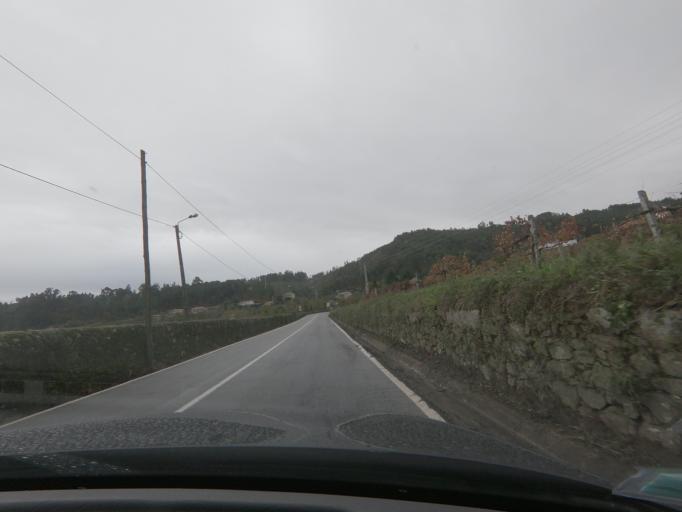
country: PT
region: Braga
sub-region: Celorico de Basto
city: Celorico de Basto
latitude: 41.4127
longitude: -7.9934
